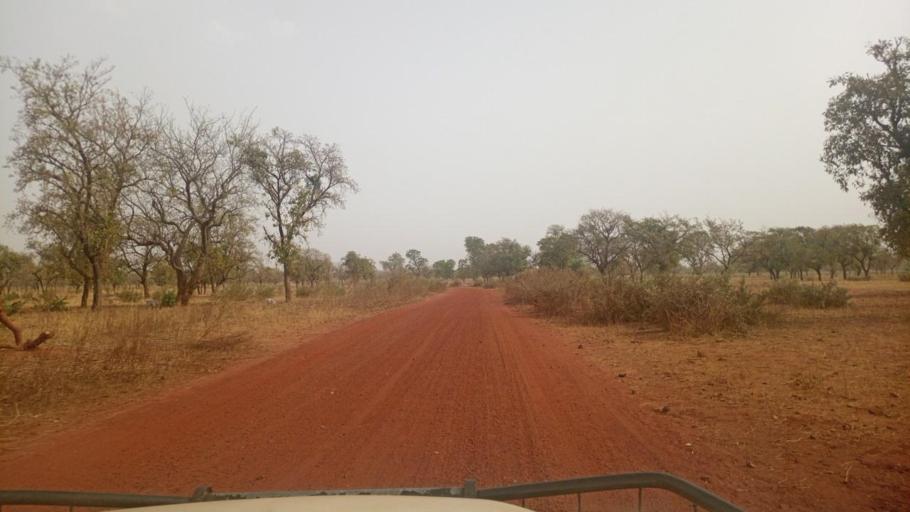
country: BF
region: Boucle du Mouhoun
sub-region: Province des Banwa
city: Salanso
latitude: 12.1011
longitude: -4.3340
